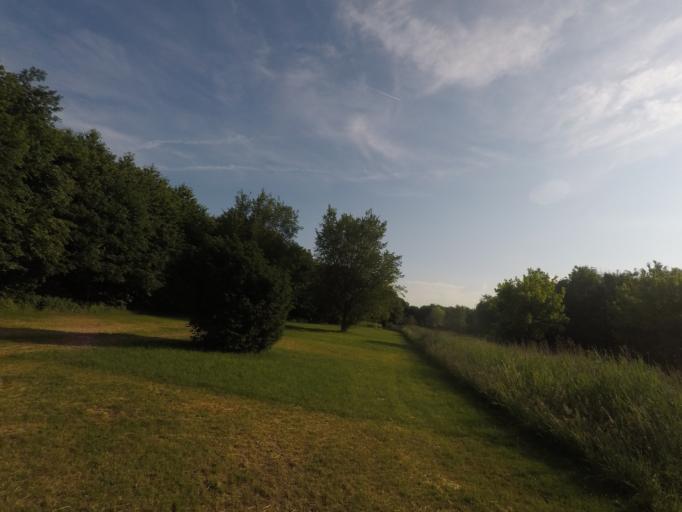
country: NL
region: Gelderland
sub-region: Gemeente Westervoort
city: Westervoort
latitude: 51.9471
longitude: 5.9915
